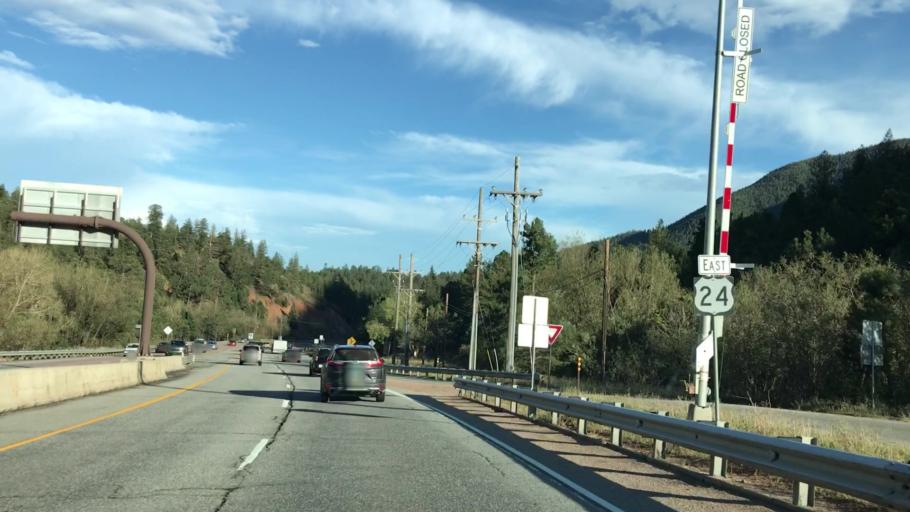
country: US
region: Colorado
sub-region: El Paso County
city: Cascade-Chipita Park
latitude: 38.8950
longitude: -104.9704
